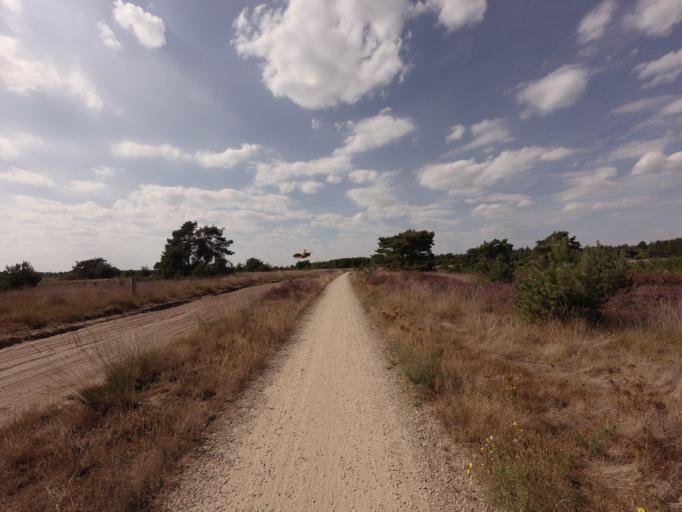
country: NL
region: North Brabant
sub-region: Gemeente Valkenswaard
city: Valkenswaard
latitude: 51.3080
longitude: 5.5144
